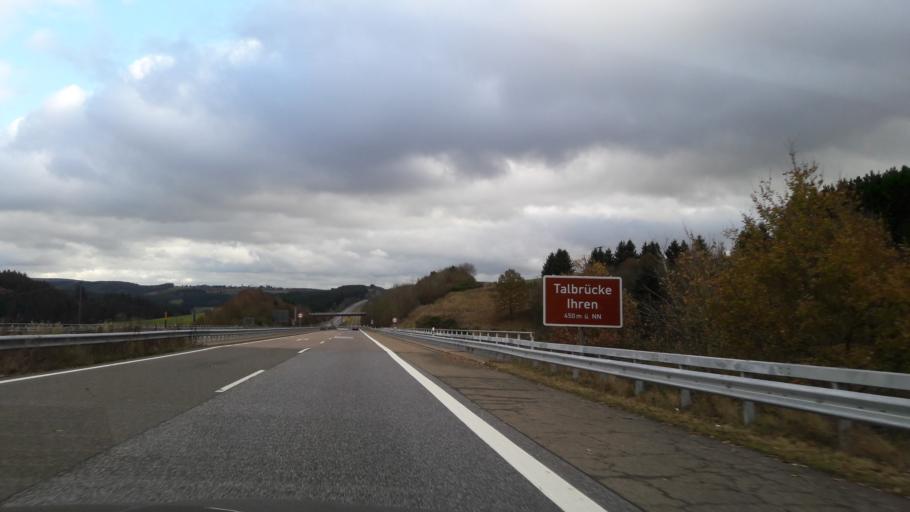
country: DE
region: Rheinland-Pfalz
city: Winterspelt
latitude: 50.2245
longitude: 6.2032
